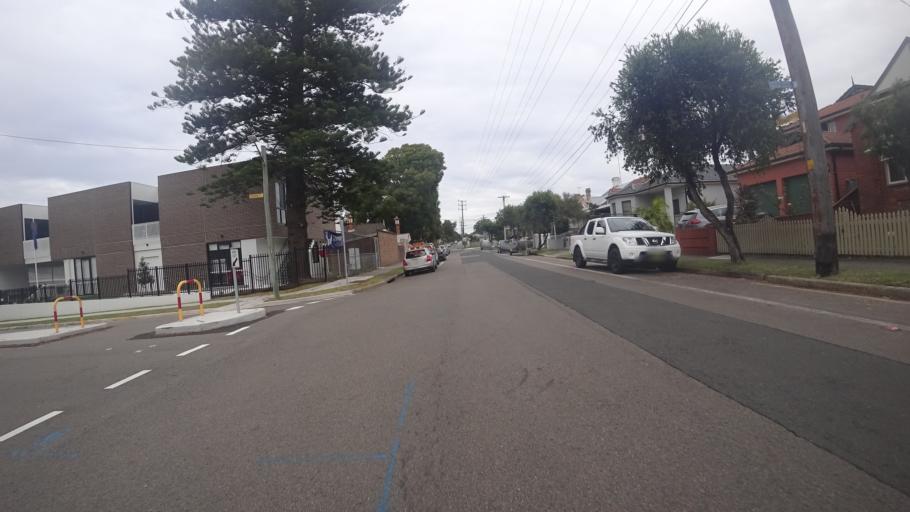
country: AU
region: New South Wales
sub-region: Rockdale
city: Bardwell Valley
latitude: -33.9357
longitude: 151.1394
